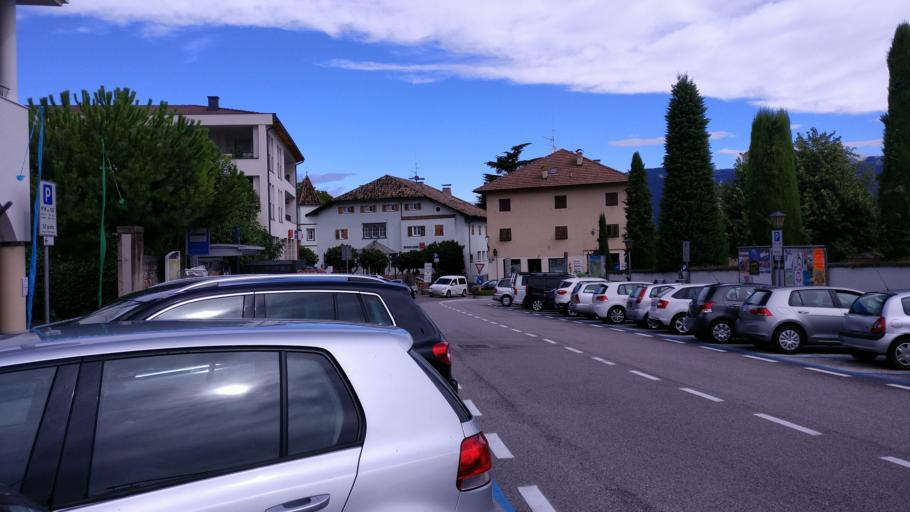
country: IT
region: Trentino-Alto Adige
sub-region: Bolzano
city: San Michele
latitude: 46.4546
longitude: 11.2603
